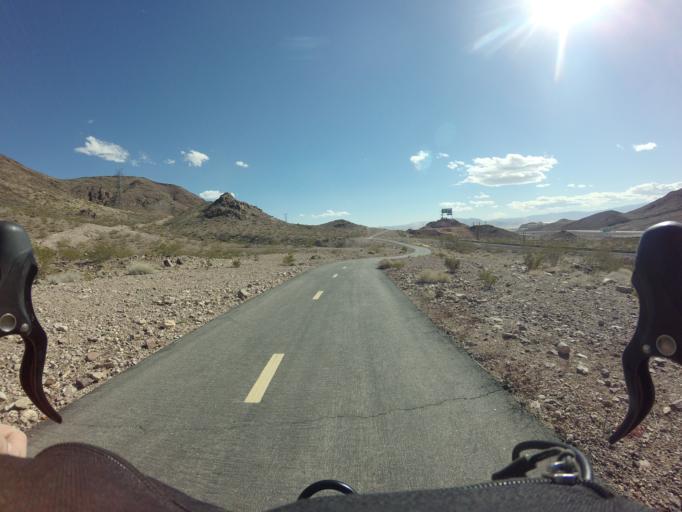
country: US
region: Nevada
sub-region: Clark County
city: Boulder City
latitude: 35.9772
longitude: -114.9128
